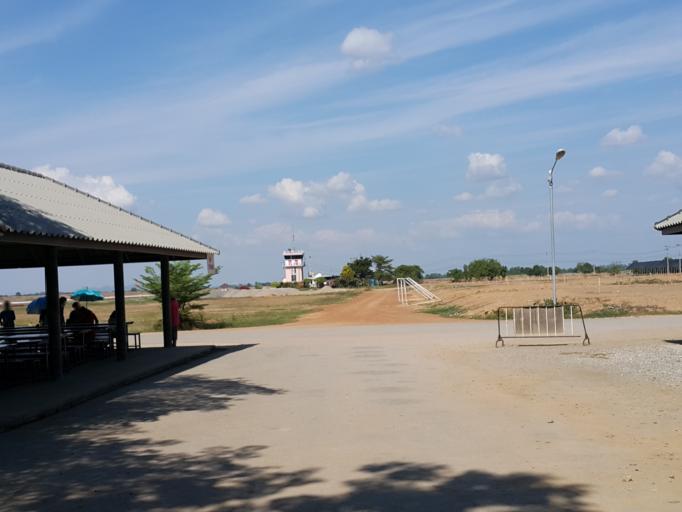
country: TH
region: Sukhothai
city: Sawankhalok
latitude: 17.2349
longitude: 99.8200
